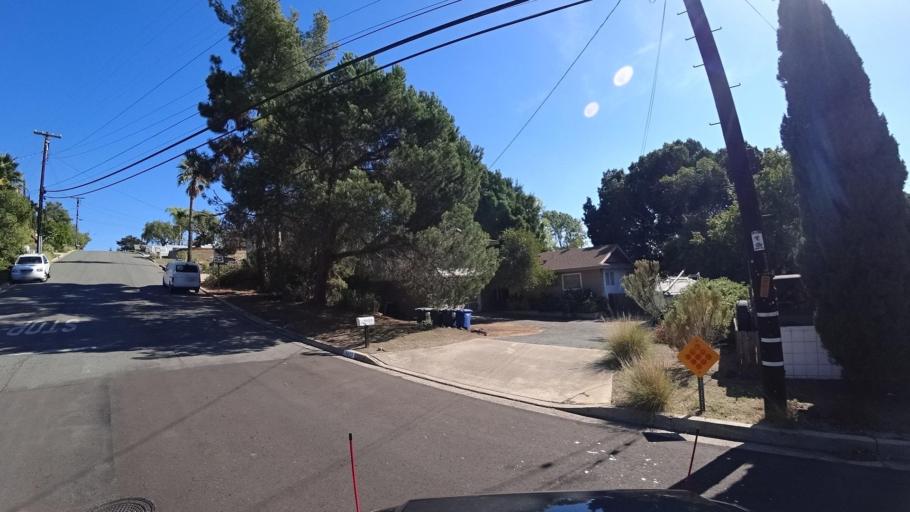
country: US
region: California
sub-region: San Diego County
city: Casa de Oro-Mount Helix
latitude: 32.7530
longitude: -116.9779
